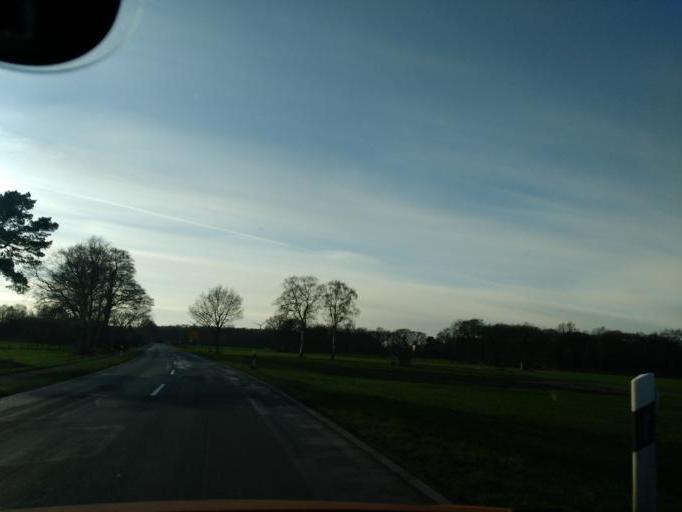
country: DE
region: Lower Saxony
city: Hatten
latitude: 53.0852
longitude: 8.3978
